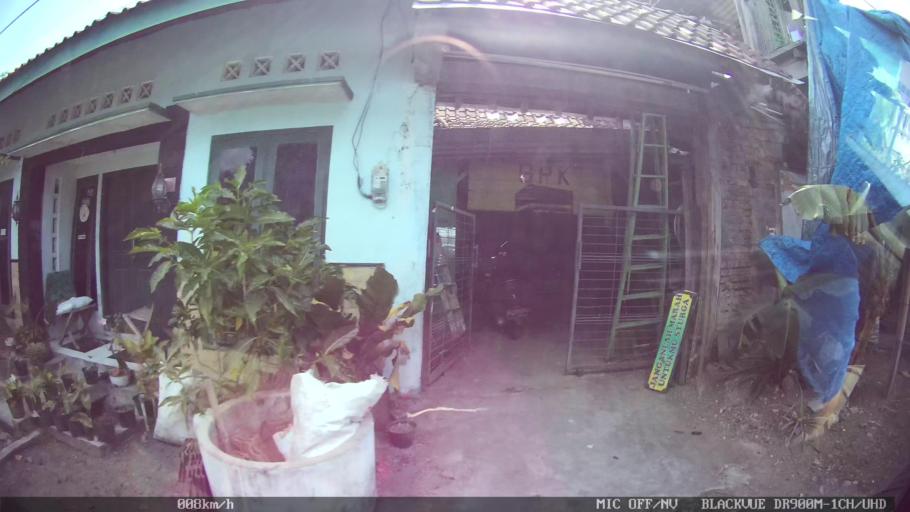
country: ID
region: Daerah Istimewa Yogyakarta
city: Kasihan
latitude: -7.8229
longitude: 110.3391
